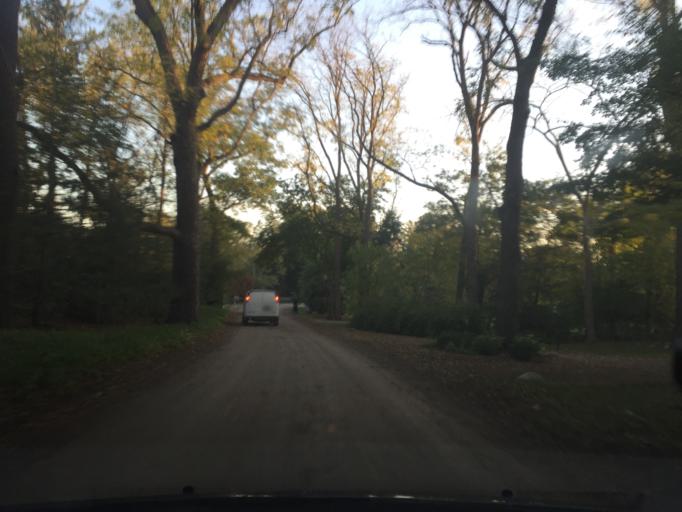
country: US
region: Michigan
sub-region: Oakland County
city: Franklin
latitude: 42.5502
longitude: -83.2938
